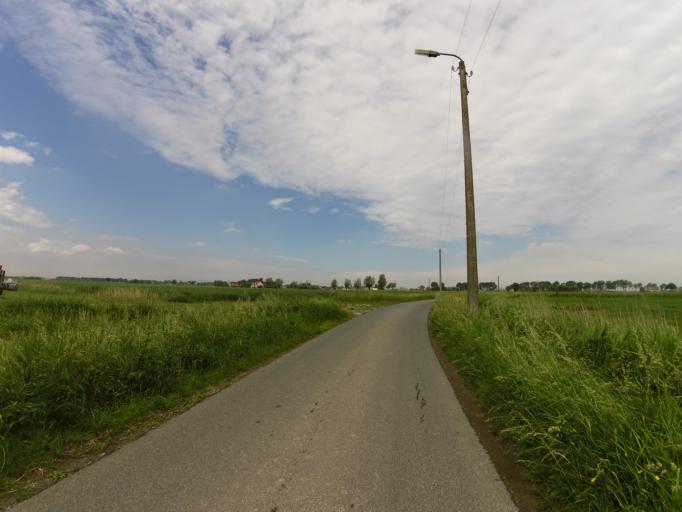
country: BE
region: Flanders
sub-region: Provincie West-Vlaanderen
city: Middelkerke
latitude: 51.1484
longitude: 2.8120
